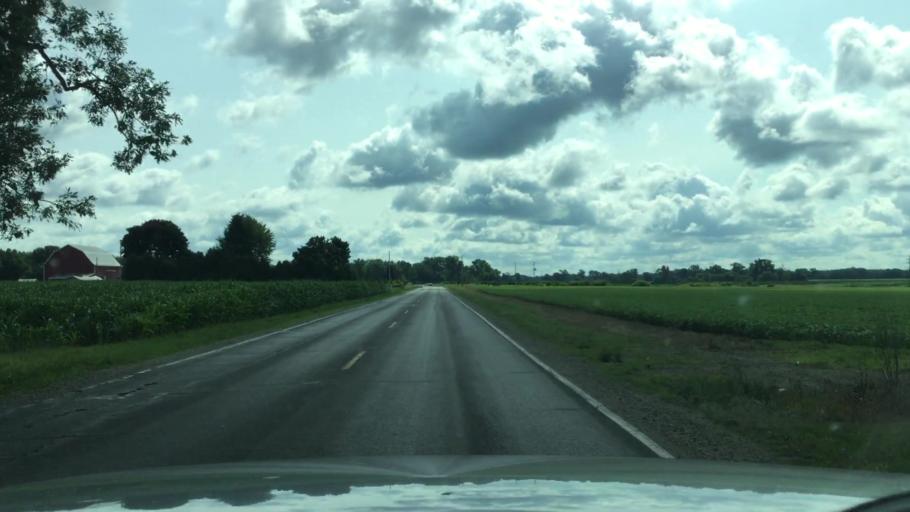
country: US
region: Michigan
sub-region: Montcalm County
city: Greenville
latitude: 43.1921
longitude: -85.1982
